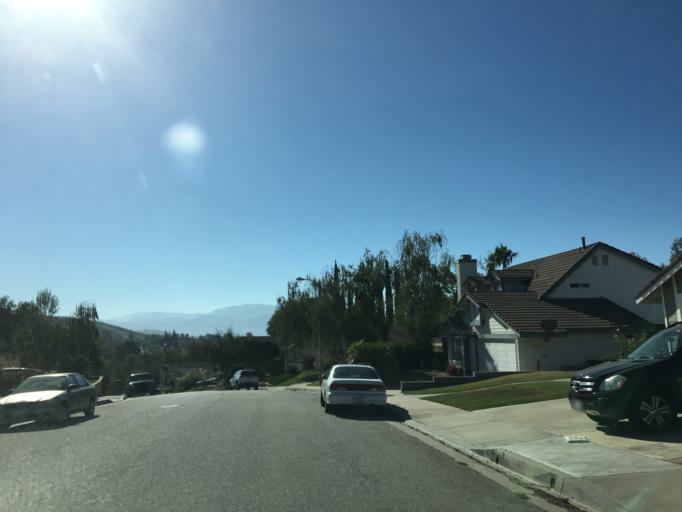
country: US
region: California
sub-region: Los Angeles County
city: Santa Clarita
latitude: 34.4386
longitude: -118.4884
